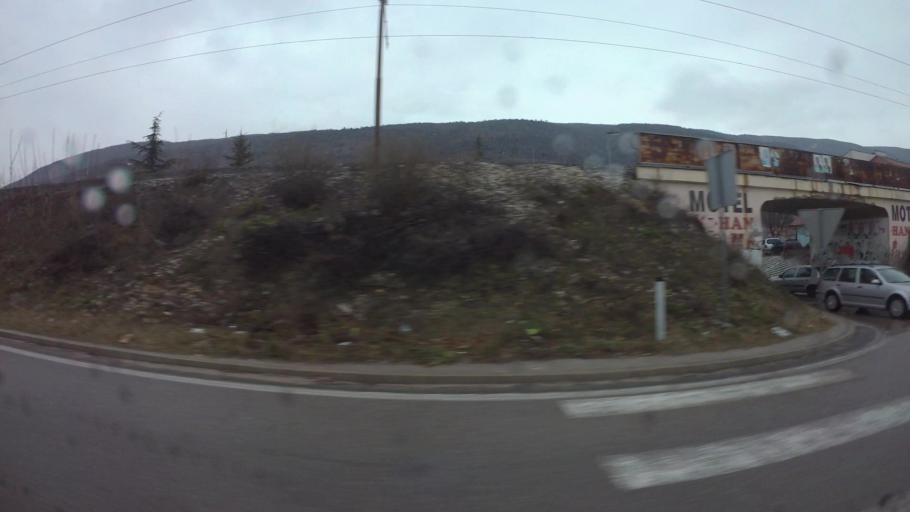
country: BA
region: Federation of Bosnia and Herzegovina
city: Rodoc
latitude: 43.3242
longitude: 17.8286
